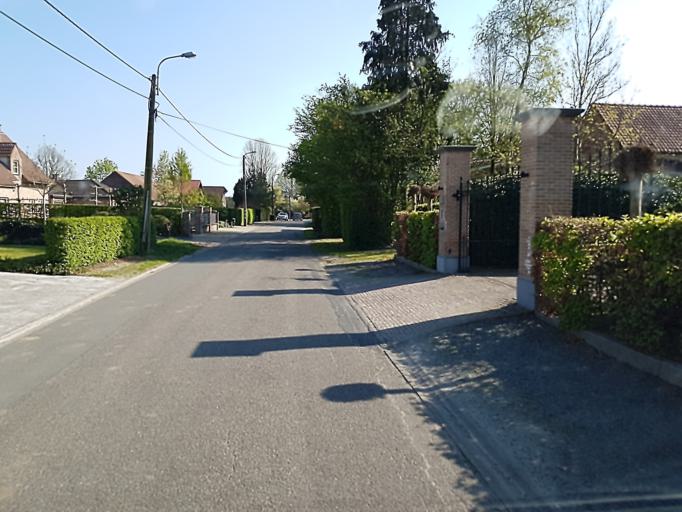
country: BE
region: Flanders
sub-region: Provincie Oost-Vlaanderen
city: Temse
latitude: 51.1386
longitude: 4.2211
